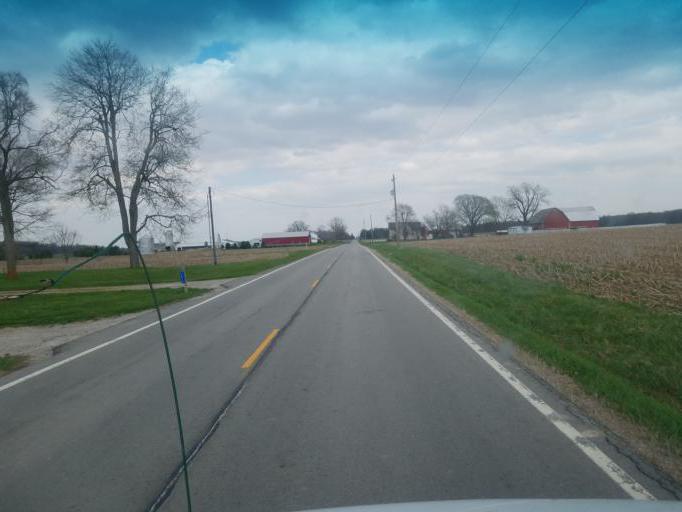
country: US
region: Ohio
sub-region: Crawford County
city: Bucyrus
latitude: 40.9504
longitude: -83.0417
